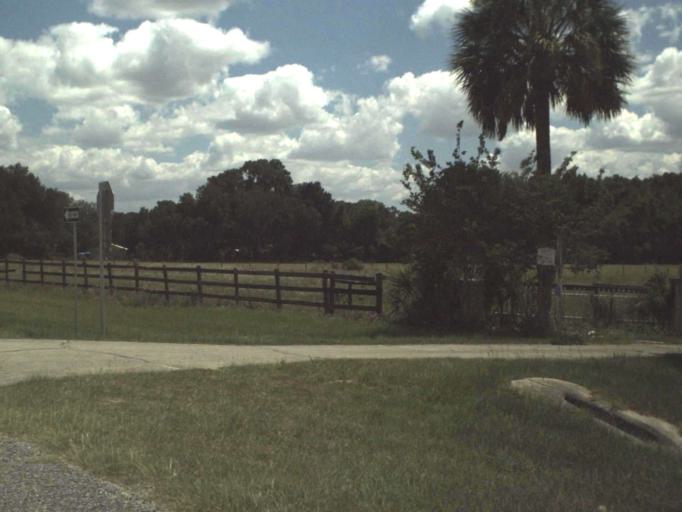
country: US
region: Florida
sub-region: Marion County
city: Citra
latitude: 29.3544
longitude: -82.1622
